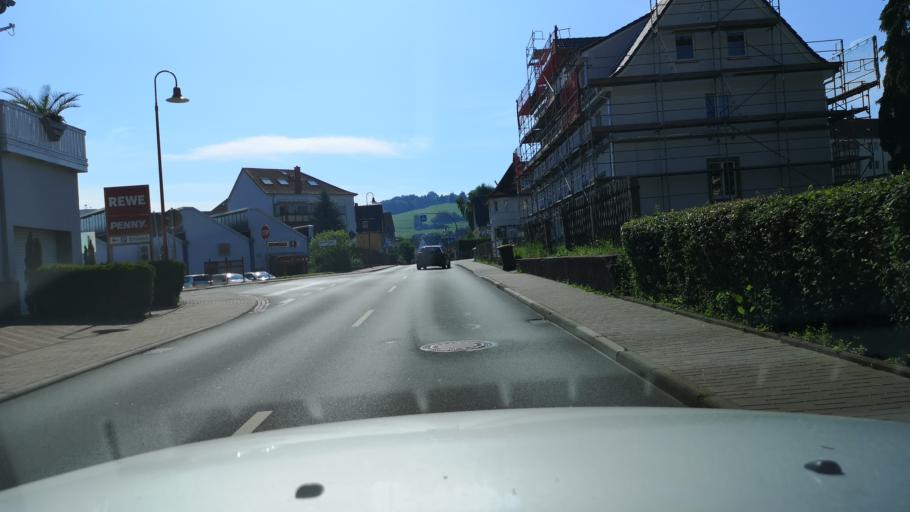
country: DE
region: Thuringia
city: Vacha
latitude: 50.8237
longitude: 10.0206
